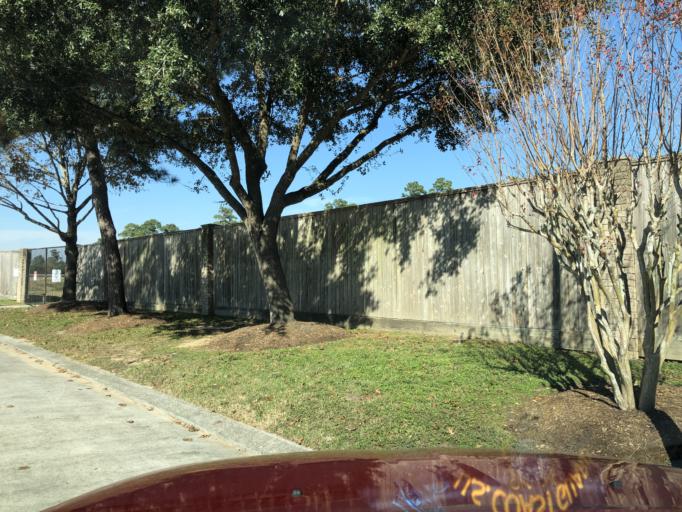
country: US
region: Texas
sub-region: Harris County
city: Tomball
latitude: 30.0340
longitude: -95.5444
